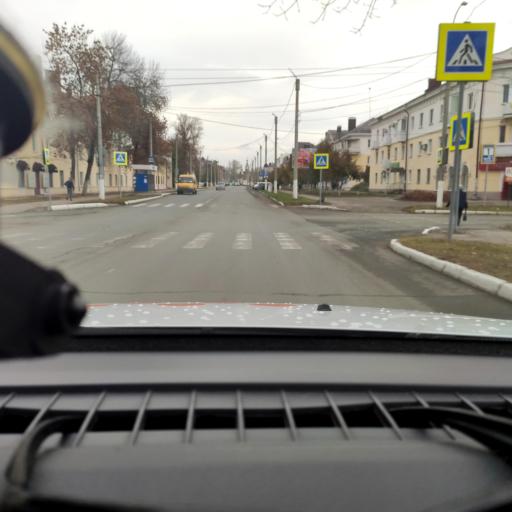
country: RU
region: Samara
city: Chapayevsk
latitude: 52.9750
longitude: 49.7099
